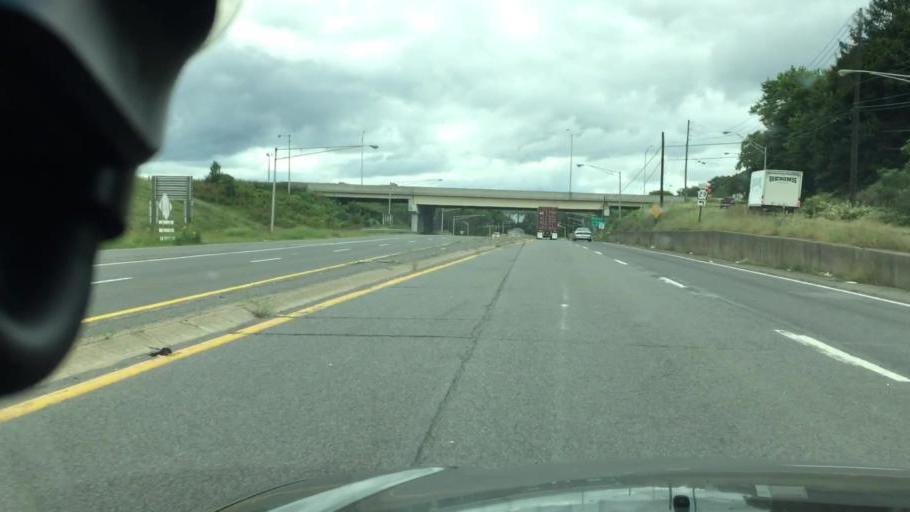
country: US
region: Pennsylvania
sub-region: Luzerne County
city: Nanticoke
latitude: 41.2092
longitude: -75.9794
